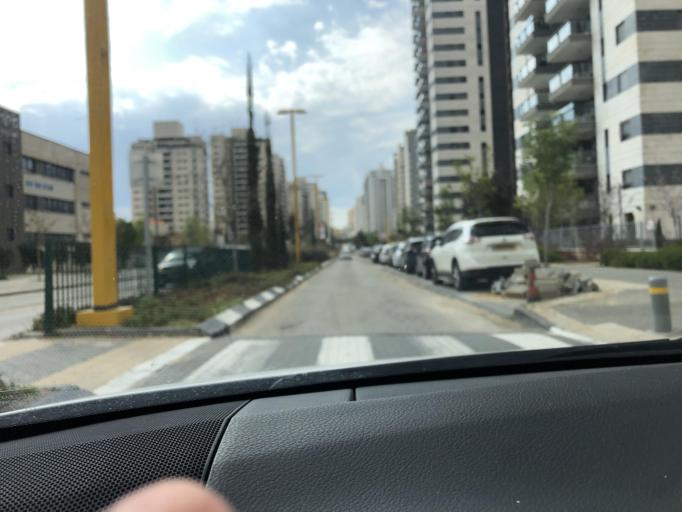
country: IL
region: Central District
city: Ganne Tiqwa
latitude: 32.0646
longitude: 34.8743
